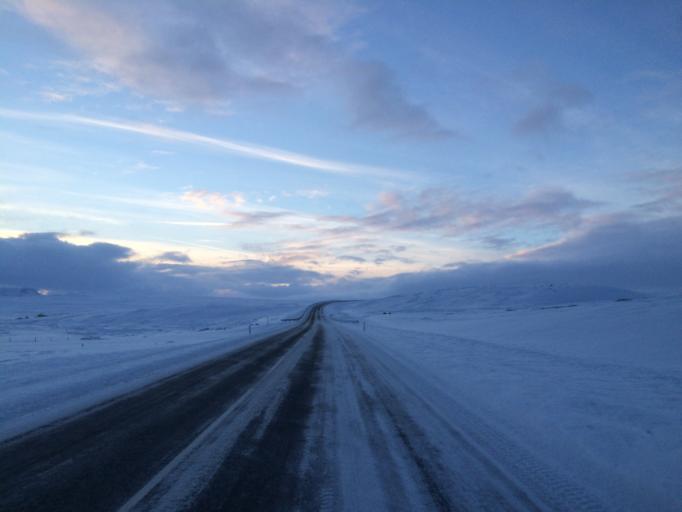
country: IS
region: South
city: Hveragerdi
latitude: 64.2266
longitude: -21.2094
